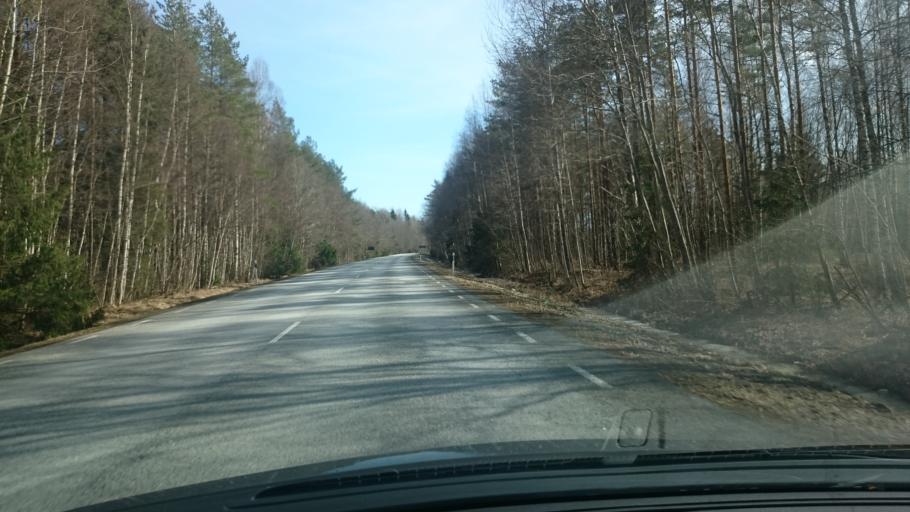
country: EE
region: Paernumaa
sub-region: Tootsi vald
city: Tootsi
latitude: 58.6637
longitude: 24.8117
